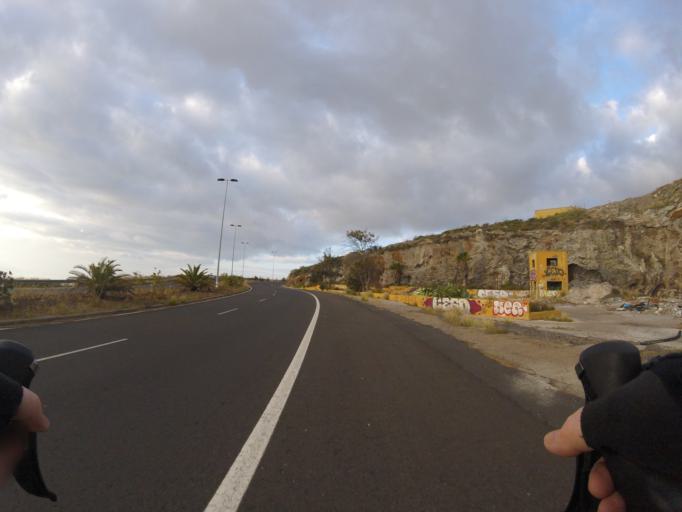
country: ES
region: Canary Islands
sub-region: Provincia de Santa Cruz de Tenerife
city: La Laguna
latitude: 28.4311
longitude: -16.3122
